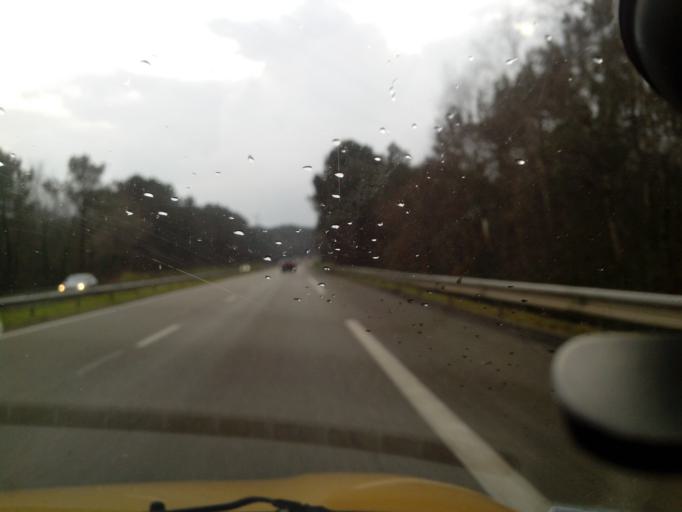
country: FR
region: Brittany
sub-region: Departement du Morbihan
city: Languidic
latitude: 47.8479
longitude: -3.1252
